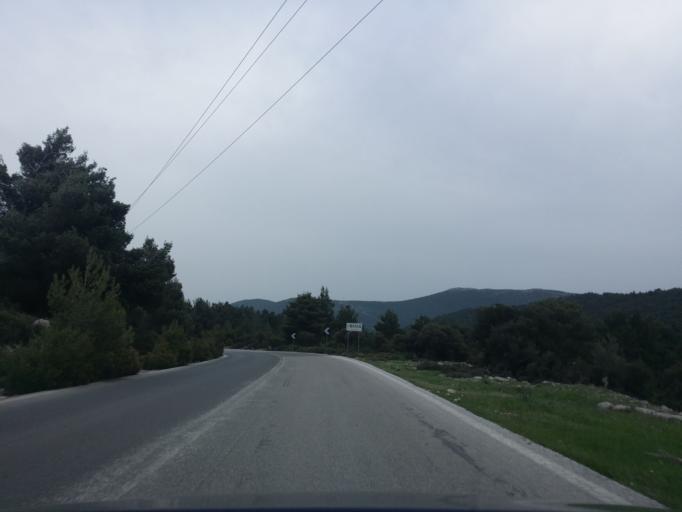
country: GR
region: Attica
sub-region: Nomarchia Dytikis Attikis
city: Vilia
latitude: 38.1673
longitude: 23.3204
